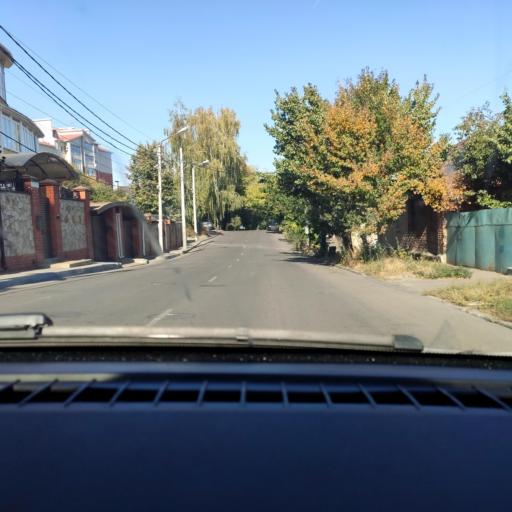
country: RU
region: Voronezj
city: Voronezh
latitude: 51.6664
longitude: 39.2144
